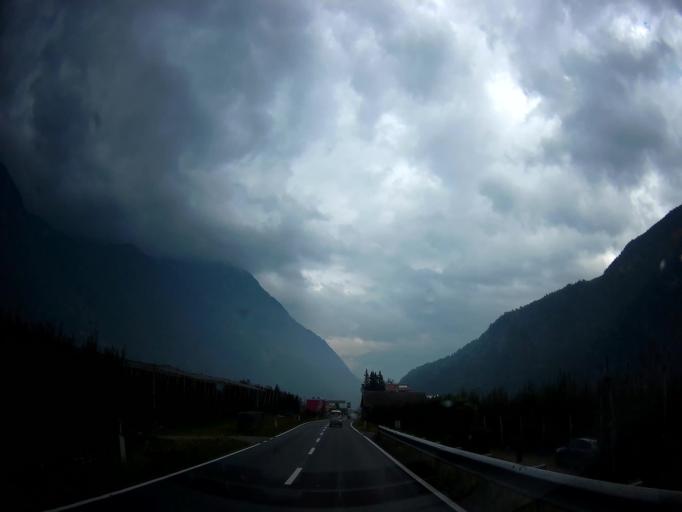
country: IT
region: Trentino-Alto Adige
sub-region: Bolzano
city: Rabla
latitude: 46.6723
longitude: 11.0727
